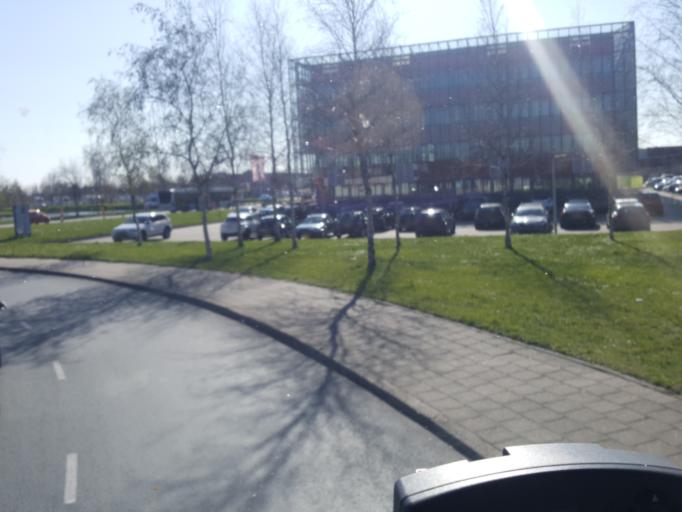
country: NL
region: North Holland
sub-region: Gemeente Aalsmeer
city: Aalsmeer
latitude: 52.2922
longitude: 4.7627
